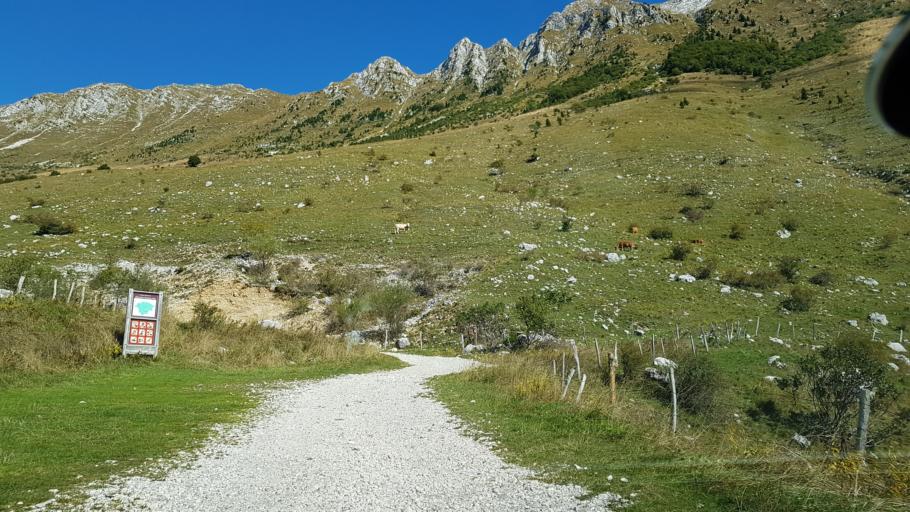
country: SI
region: Kobarid
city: Kobarid
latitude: 46.2830
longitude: 13.6306
